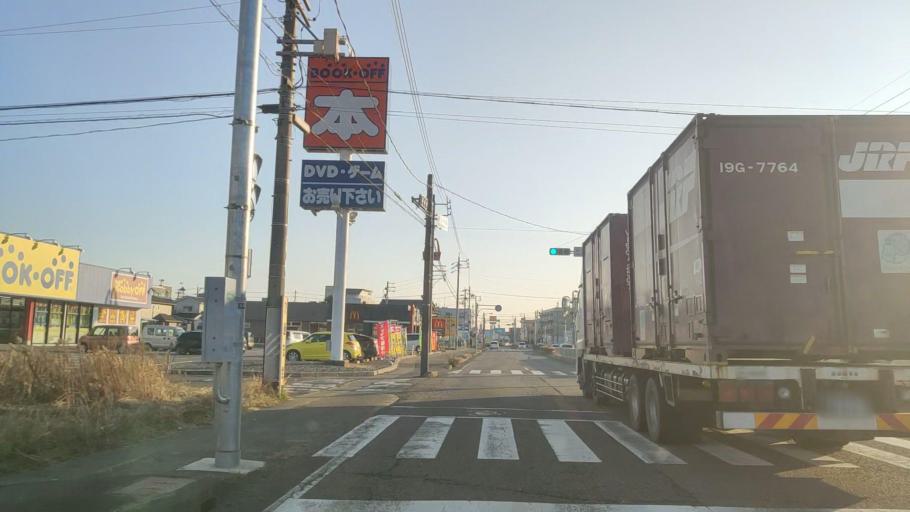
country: JP
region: Gifu
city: Gifu-shi
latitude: 35.4473
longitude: 136.7405
